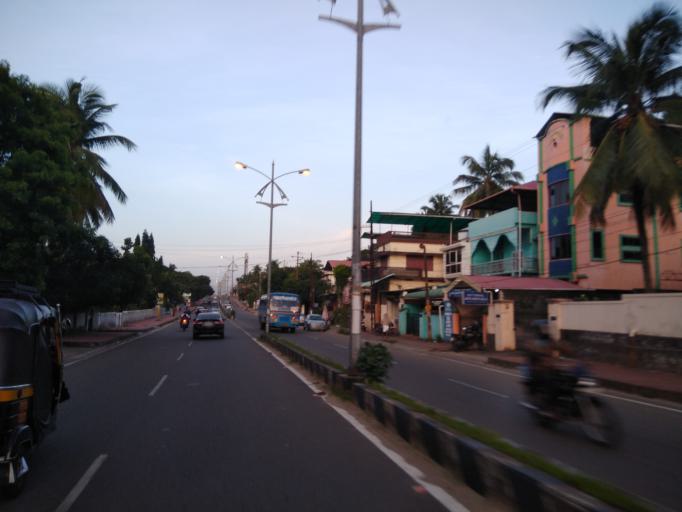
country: IN
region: Kerala
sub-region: Thrissur District
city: Trichur
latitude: 10.5212
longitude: 76.1933
